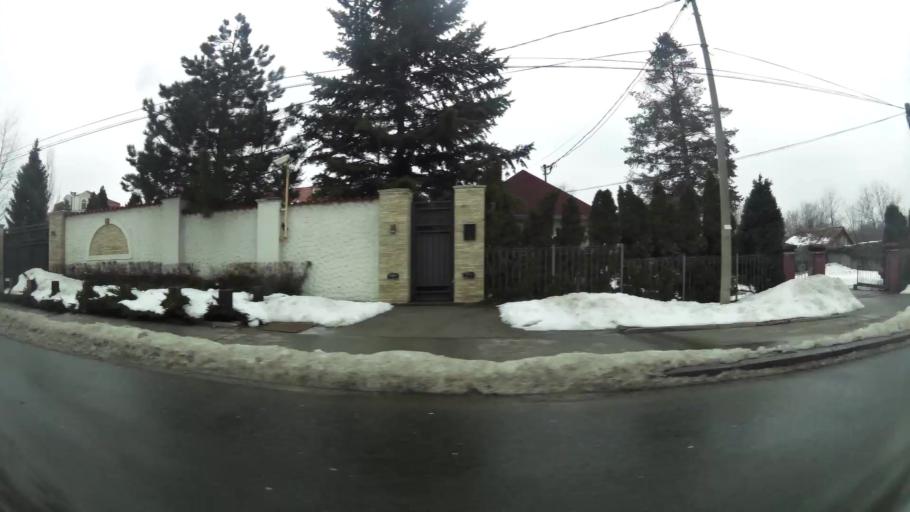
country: RS
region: Central Serbia
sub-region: Belgrade
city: Vozdovac
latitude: 44.7569
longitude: 20.4875
